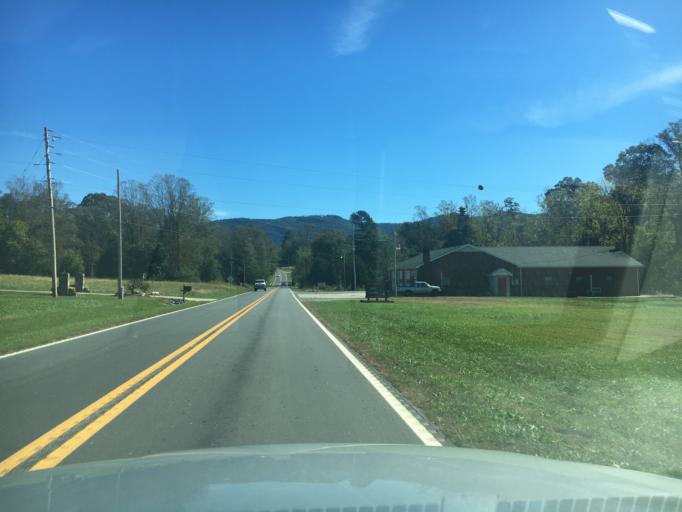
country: US
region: North Carolina
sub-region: Burke County
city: Glen Alpine
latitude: 35.6428
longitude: -81.7817
